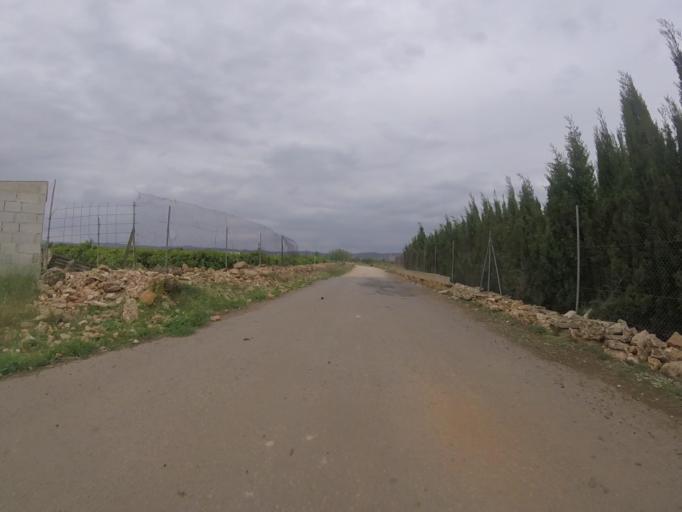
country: ES
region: Valencia
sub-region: Provincia de Castello
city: Torreblanca
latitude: 40.2166
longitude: 0.2303
